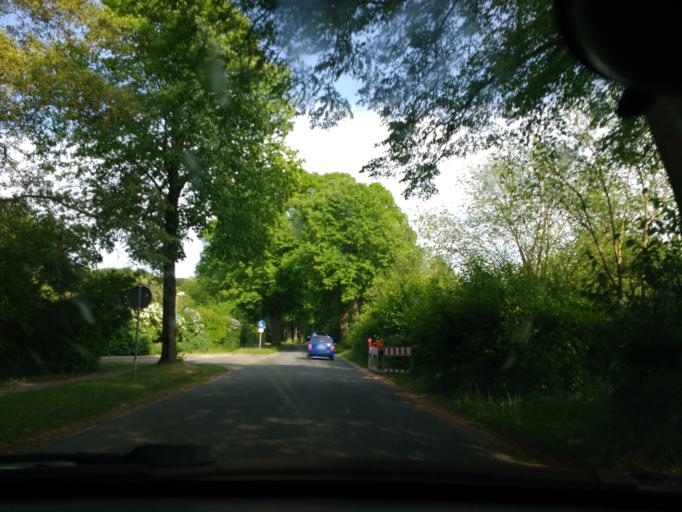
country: DE
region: Schleswig-Holstein
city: Einhaus
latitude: 53.7107
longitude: 10.7395
